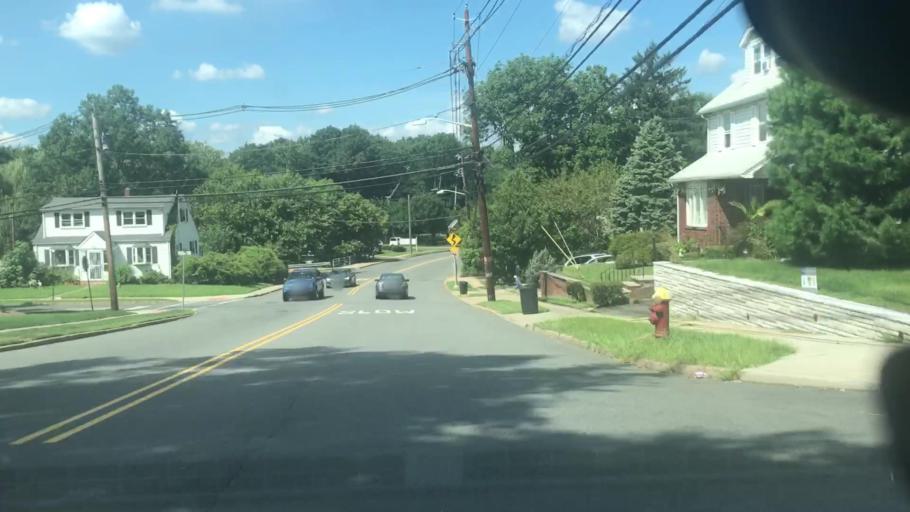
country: US
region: New Jersey
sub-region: Essex County
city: Bloomfield
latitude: 40.8039
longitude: -74.1713
